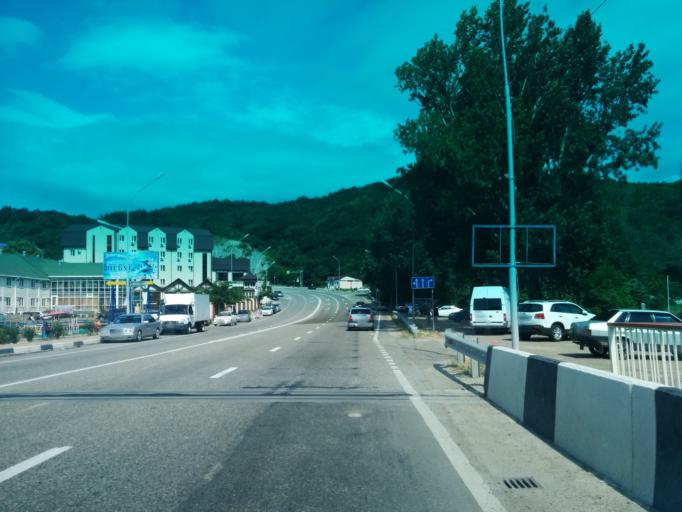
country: RU
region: Krasnodarskiy
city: Nebug
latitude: 44.1653
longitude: 39.0004
